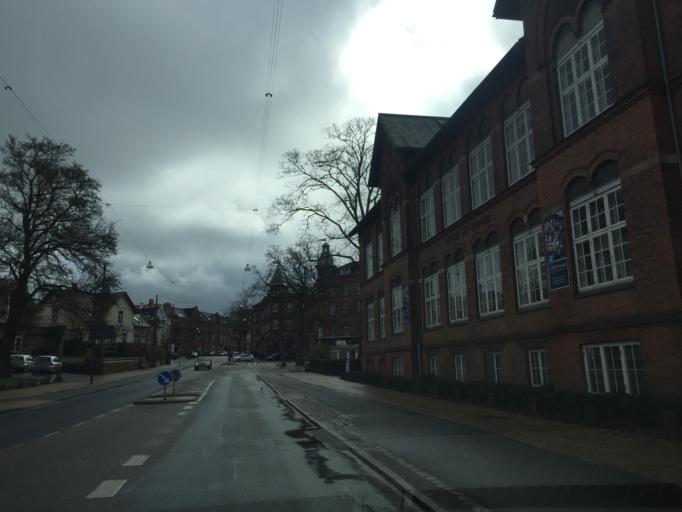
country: DK
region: South Denmark
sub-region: Odense Kommune
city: Odense
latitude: 55.3919
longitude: 10.3874
